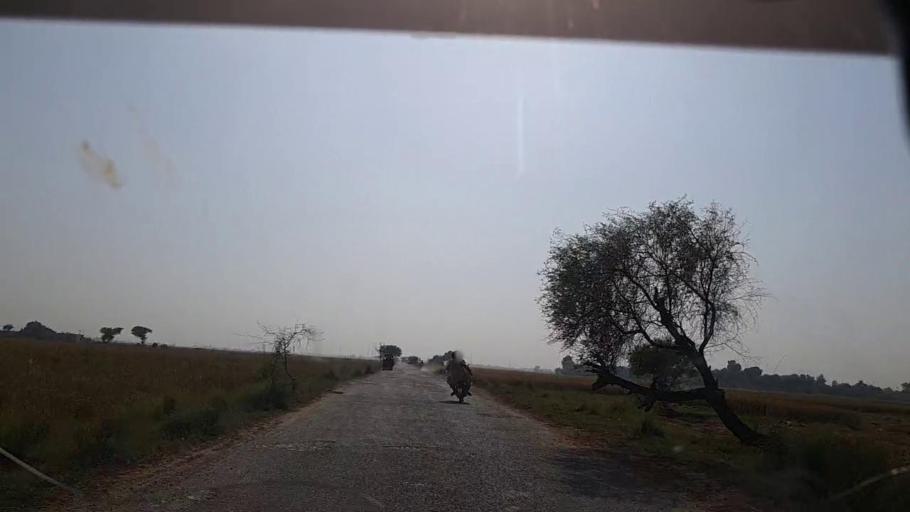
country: PK
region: Sindh
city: Shikarpur
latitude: 28.0926
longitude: 68.6082
